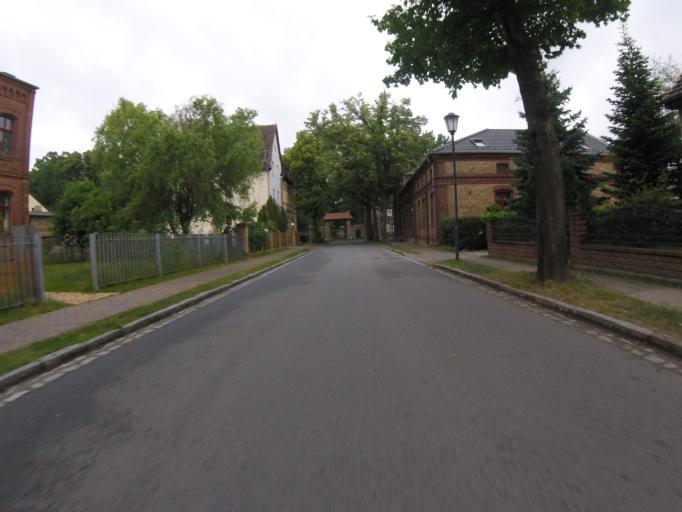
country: DE
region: Brandenburg
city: Konigs Wusterhausen
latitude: 52.2779
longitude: 13.5982
